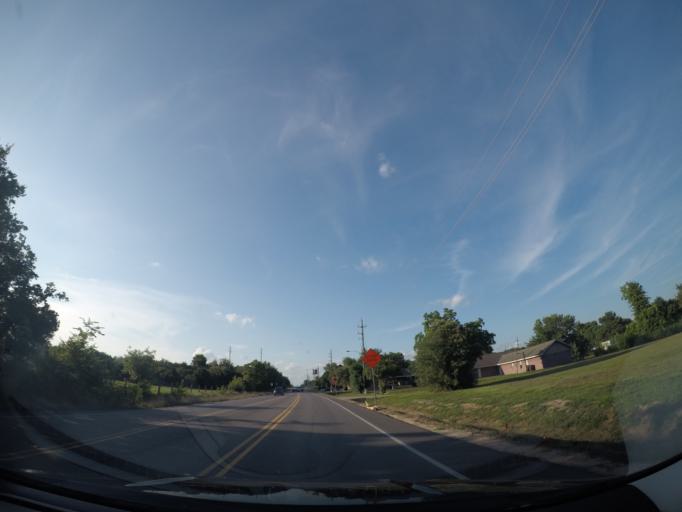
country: US
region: Texas
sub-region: Waller County
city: Brookshire
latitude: 29.7751
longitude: -95.9675
